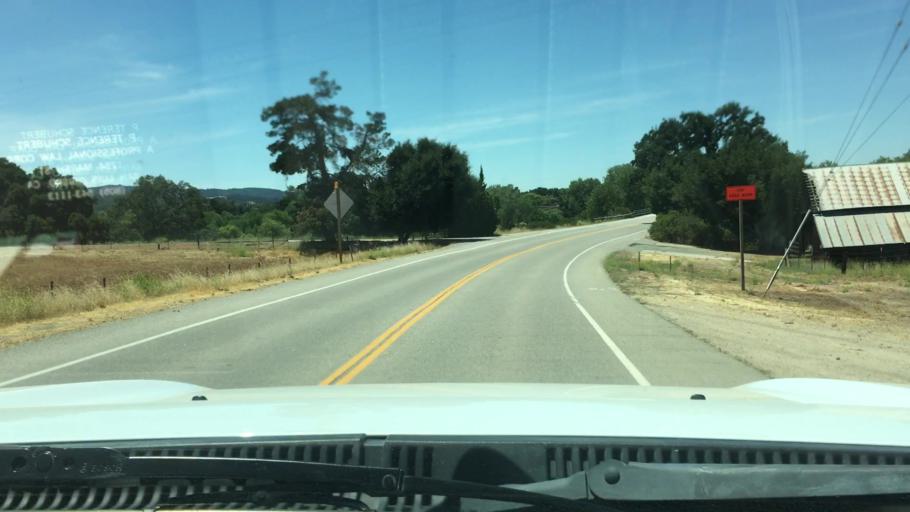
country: US
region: California
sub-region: San Luis Obispo County
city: Templeton
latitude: 35.5431
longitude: -120.7049
